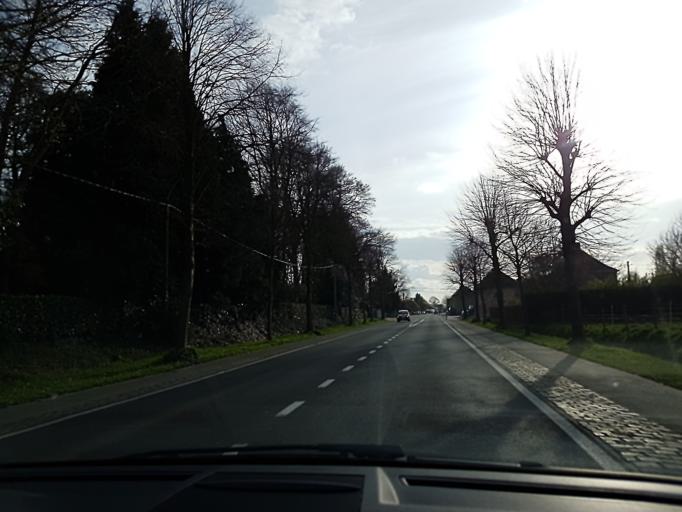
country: BE
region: Flanders
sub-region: Provincie West-Vlaanderen
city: Zedelgem
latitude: 51.1531
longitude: 3.1806
